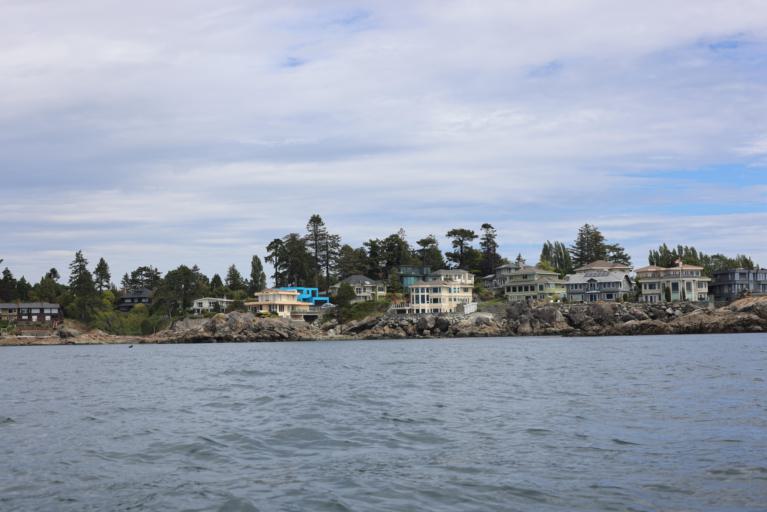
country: CA
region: British Columbia
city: Victoria
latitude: 48.4190
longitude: -123.4178
